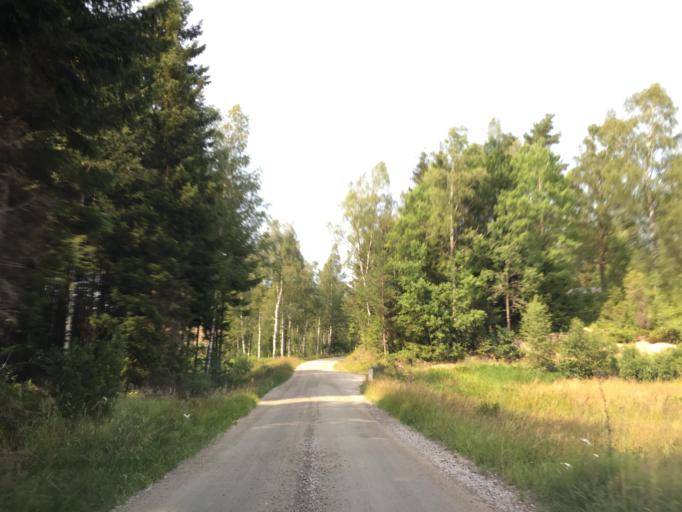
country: SE
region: Vaestra Goetaland
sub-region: Lilla Edets Kommun
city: Lilla Edet
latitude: 58.2428
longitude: 12.0824
